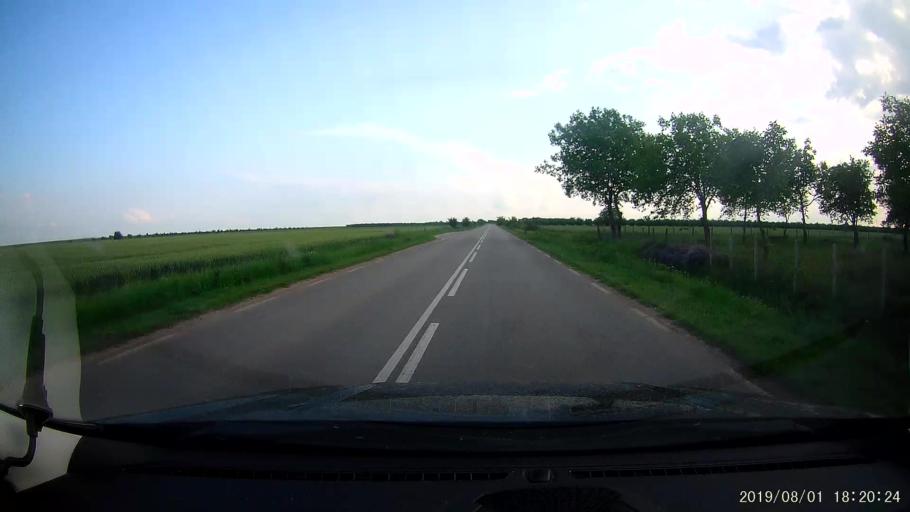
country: BG
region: Shumen
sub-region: Obshtina Kaolinovo
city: Kaolinovo
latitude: 43.6719
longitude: 27.0890
